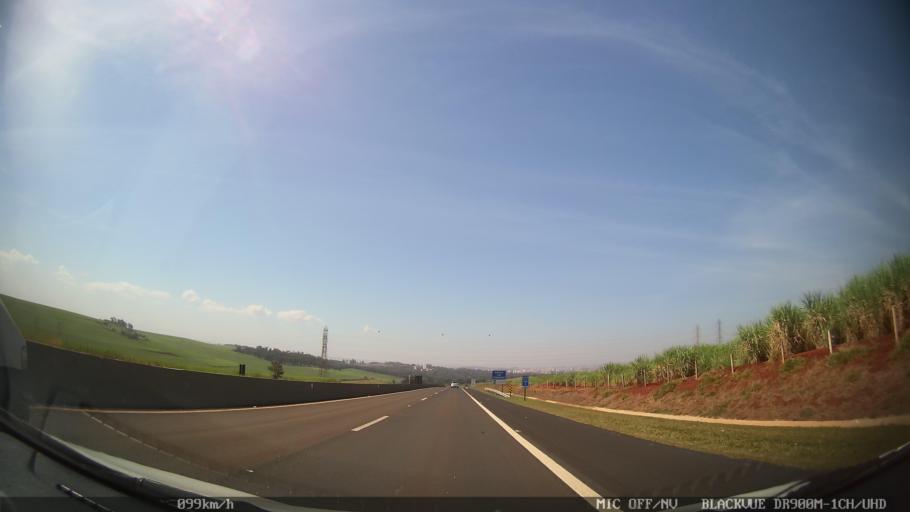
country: BR
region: Sao Paulo
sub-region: Ribeirao Preto
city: Ribeirao Preto
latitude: -21.1662
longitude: -47.8907
